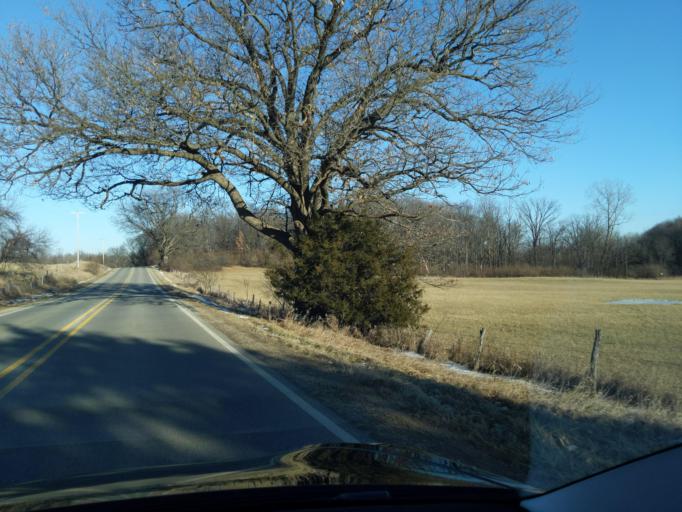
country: US
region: Michigan
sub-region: Ingham County
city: Stockbridge
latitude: 42.4160
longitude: -84.1827
